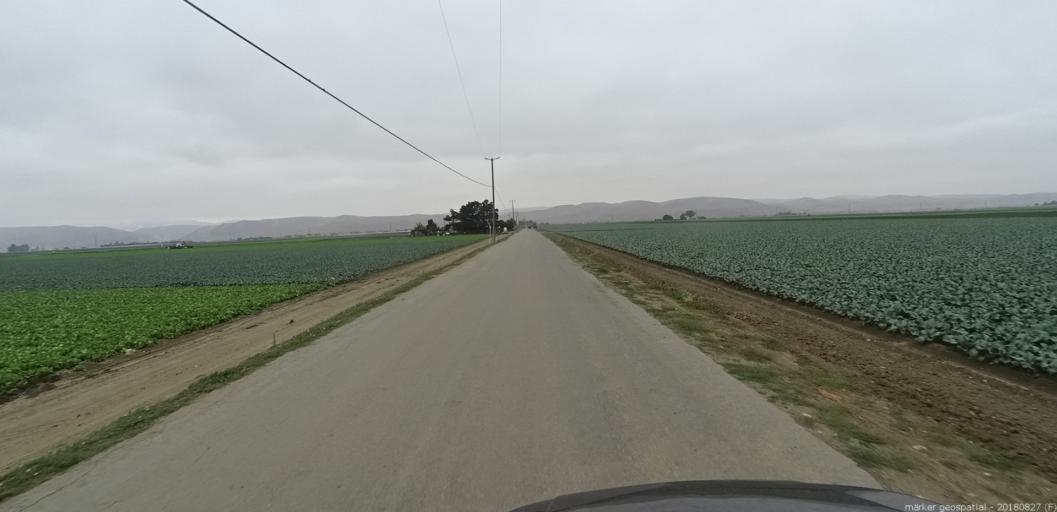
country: US
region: California
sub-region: Monterey County
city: Greenfield
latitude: 36.3141
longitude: -121.2195
